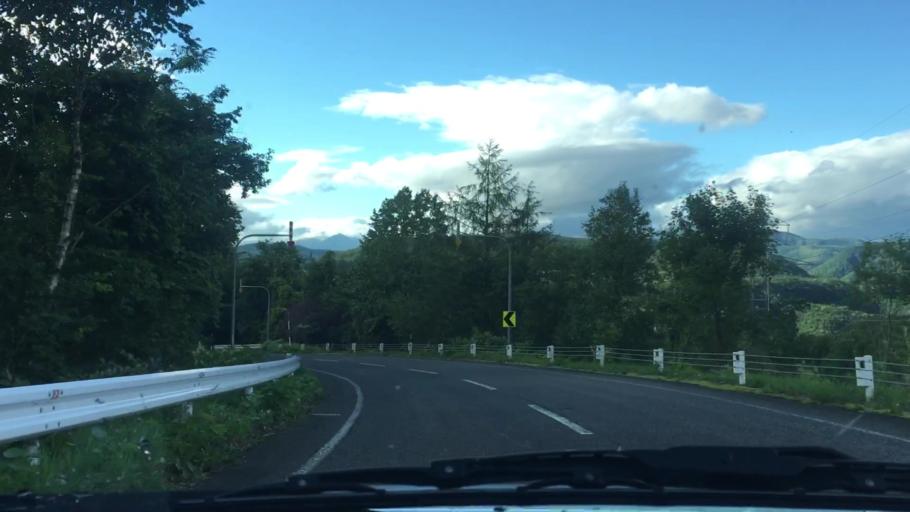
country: JP
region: Hokkaido
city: Otofuke
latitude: 43.1747
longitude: 142.9292
